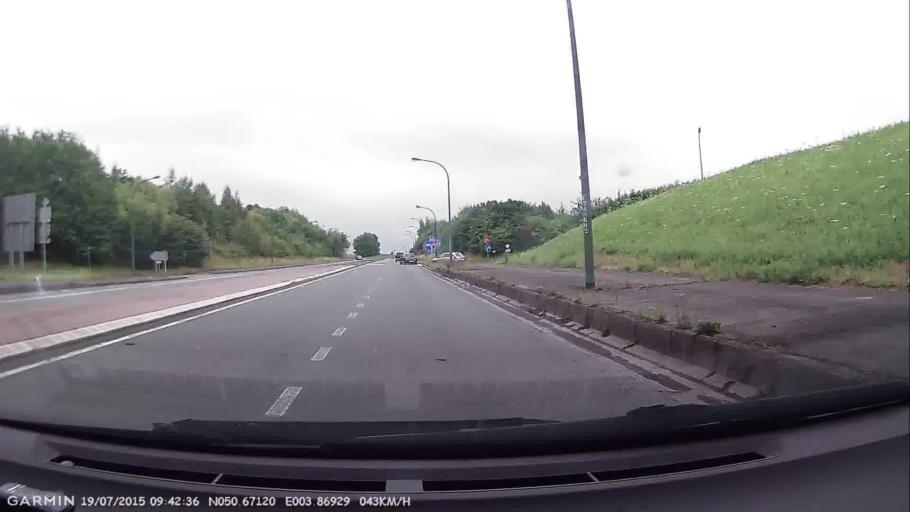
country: BE
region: Wallonia
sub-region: Province du Hainaut
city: Lessines
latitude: 50.6712
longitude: 3.8692
